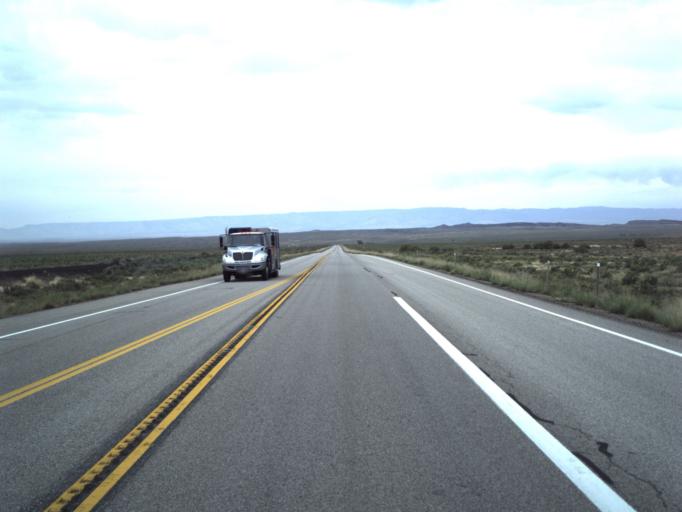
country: US
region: Utah
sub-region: Carbon County
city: East Carbon City
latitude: 39.5338
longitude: -110.5258
